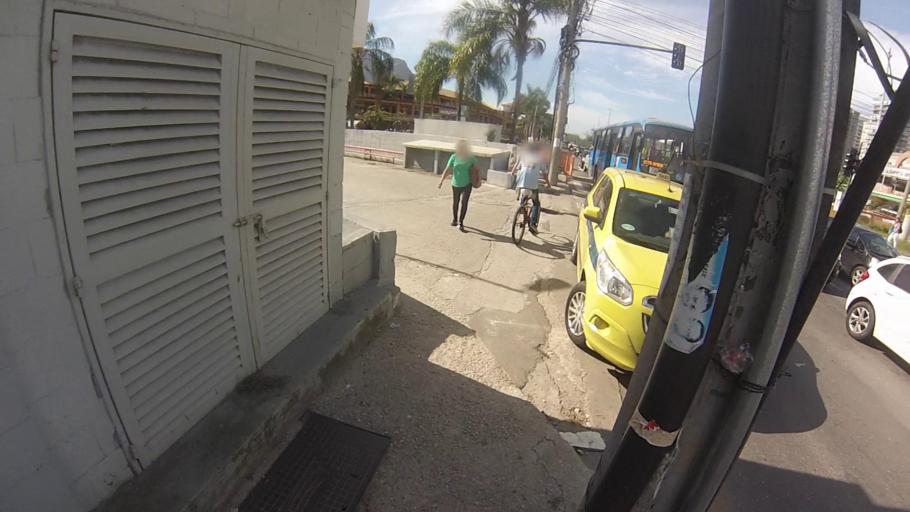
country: BR
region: Rio de Janeiro
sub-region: Rio De Janeiro
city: Rio de Janeiro
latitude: -23.0030
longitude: -43.3237
